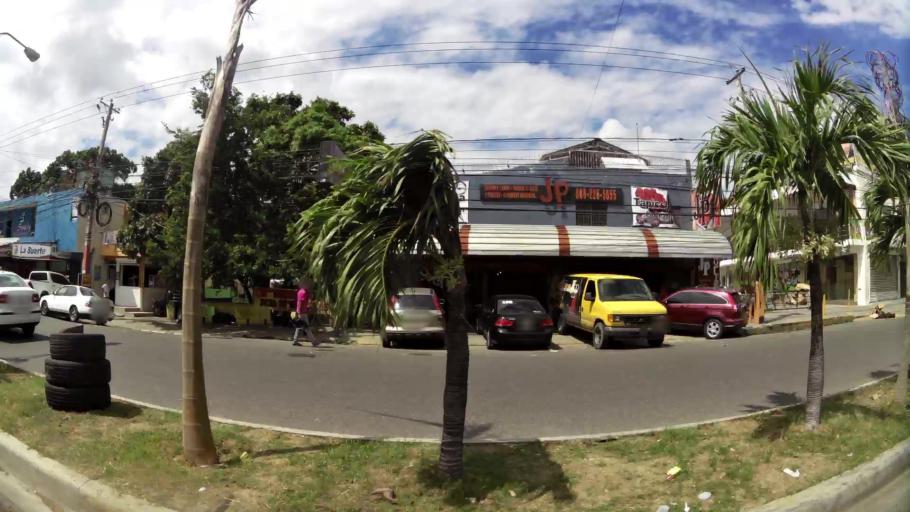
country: DO
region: Santiago
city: Santiago de los Caballeros
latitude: 19.4634
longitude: -70.7108
